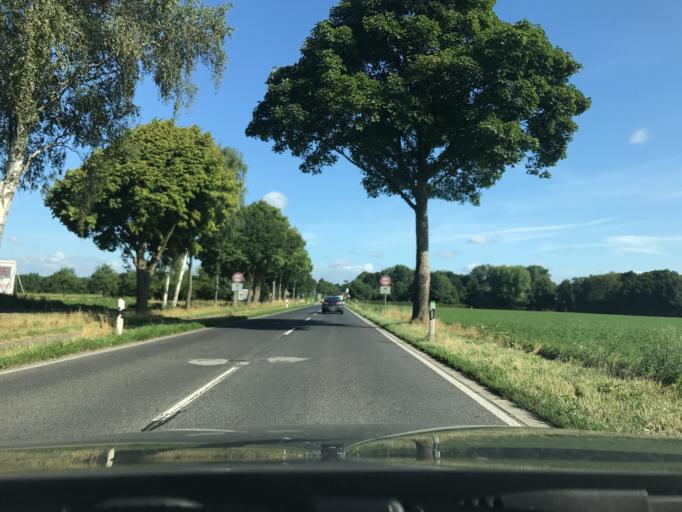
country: DE
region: North Rhine-Westphalia
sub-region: Regierungsbezirk Dusseldorf
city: Grefrath
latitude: 51.3577
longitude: 6.3178
